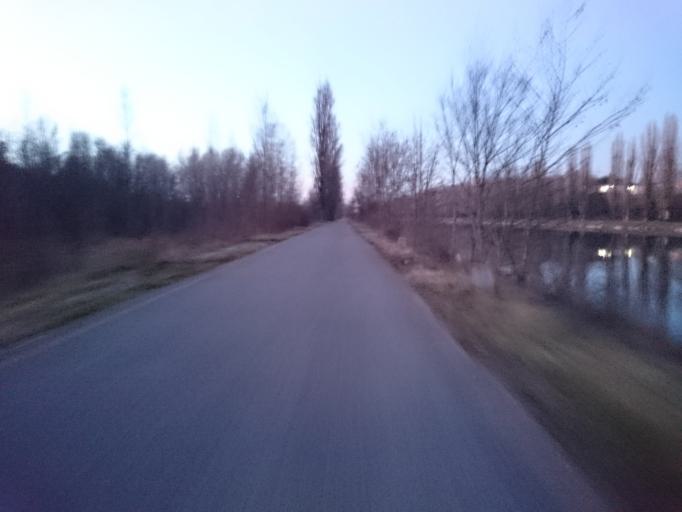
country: IT
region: Veneto
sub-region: Provincia di Verona
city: Salionze
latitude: 45.4094
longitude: 10.7167
